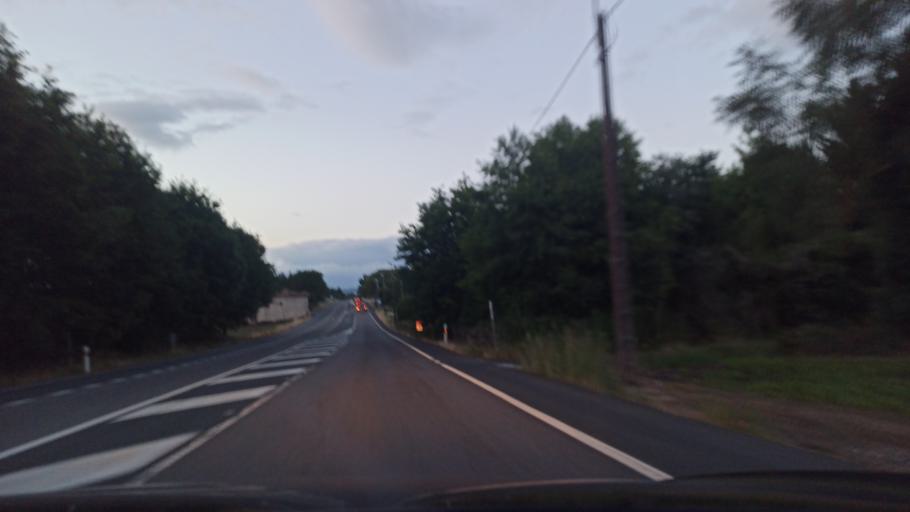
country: ES
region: Galicia
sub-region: Provincia de Lugo
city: Lugo
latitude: 42.9701
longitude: -7.5952
